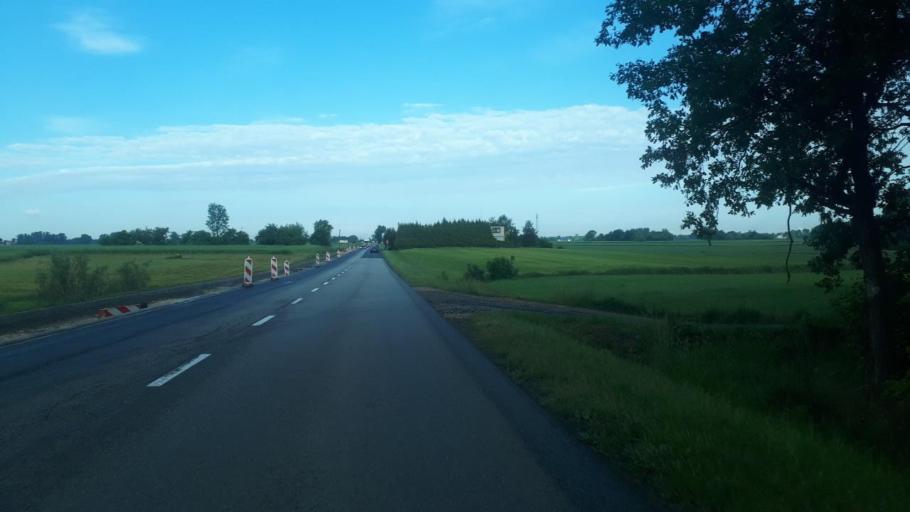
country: PL
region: Silesian Voivodeship
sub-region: Powiat pszczynski
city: Jankowice
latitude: 49.9709
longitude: 19.0124
